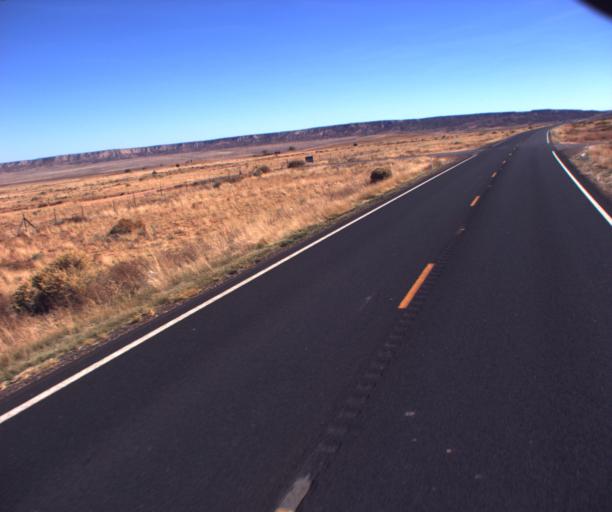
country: US
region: Arizona
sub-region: Apache County
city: Ganado
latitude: 35.7805
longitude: -109.6602
